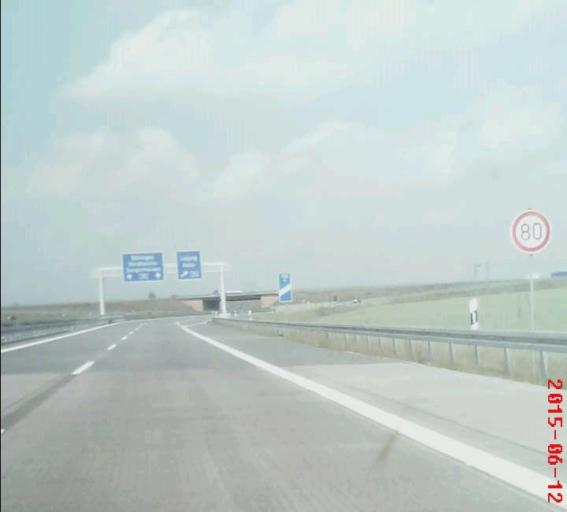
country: DE
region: Saxony-Anhalt
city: Oberroblingen
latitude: 51.4355
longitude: 11.3299
